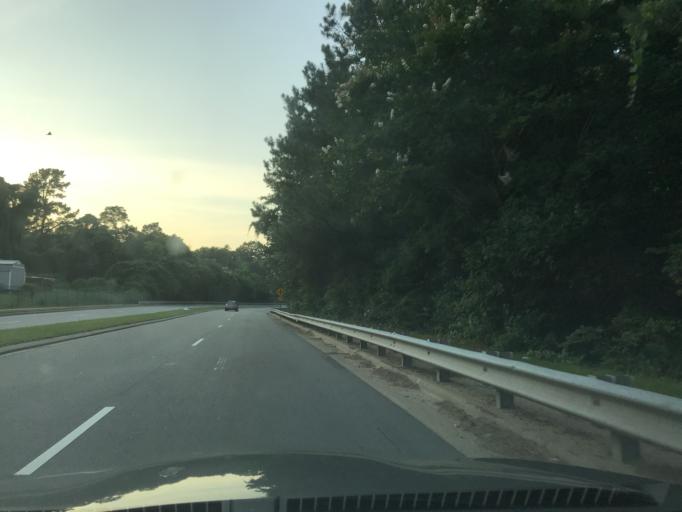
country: US
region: North Carolina
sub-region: Wake County
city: Raleigh
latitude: 35.7751
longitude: -78.6136
